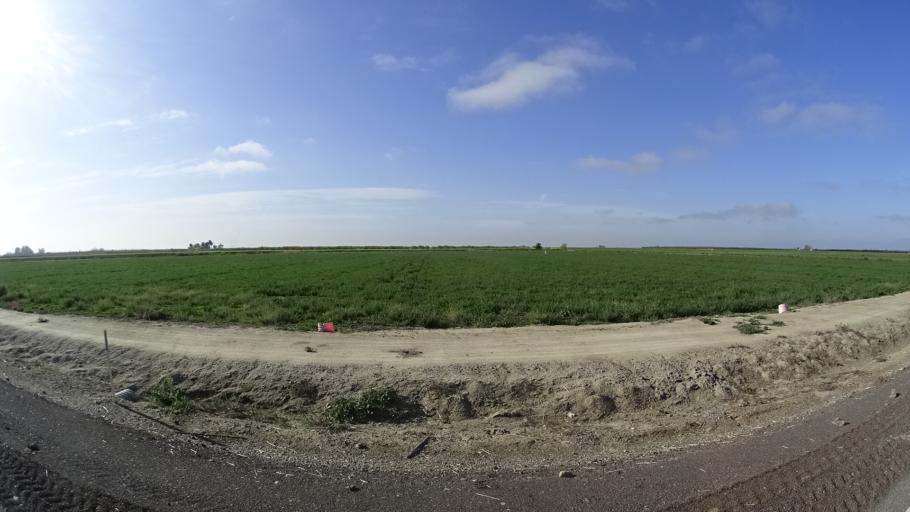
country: US
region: California
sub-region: Glenn County
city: Willows
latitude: 39.5821
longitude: -122.1265
